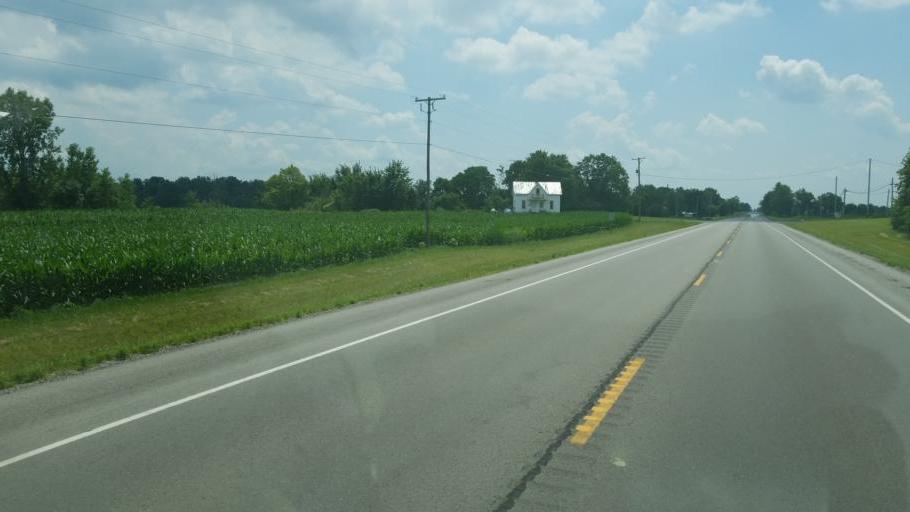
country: US
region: Ohio
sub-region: Hardin County
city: Kenton
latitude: 40.5931
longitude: -83.6401
